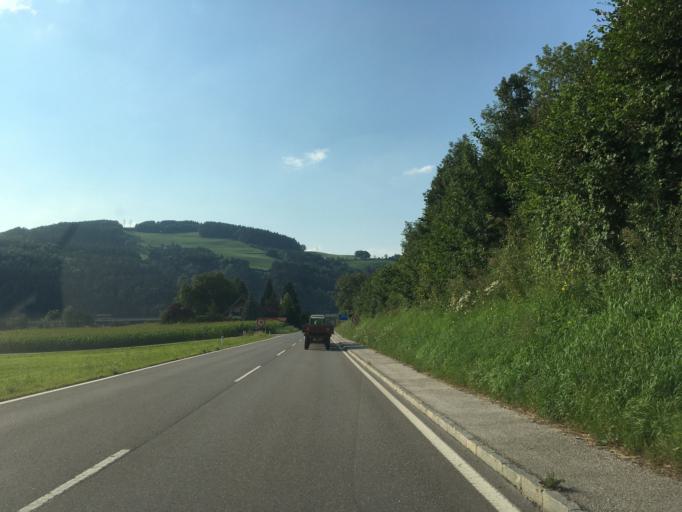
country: AT
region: Lower Austria
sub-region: Politischer Bezirk Neunkirchen
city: Grimmenstein
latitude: 47.6064
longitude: 16.1281
